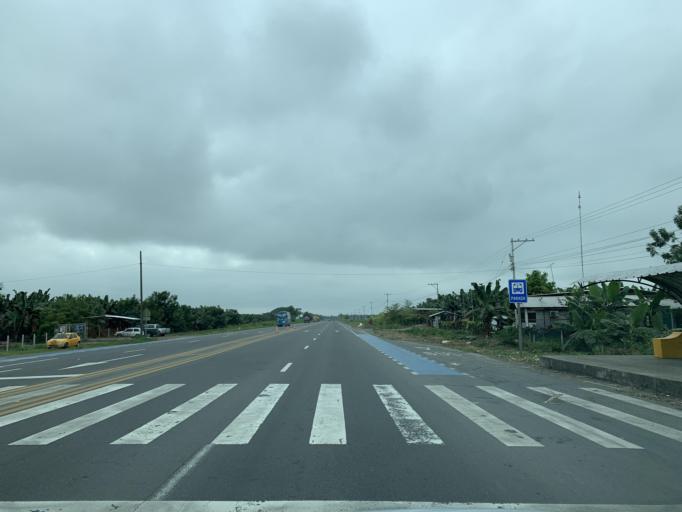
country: EC
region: Guayas
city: Coronel Marcelino Mariduena
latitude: -2.2948
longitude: -79.4993
